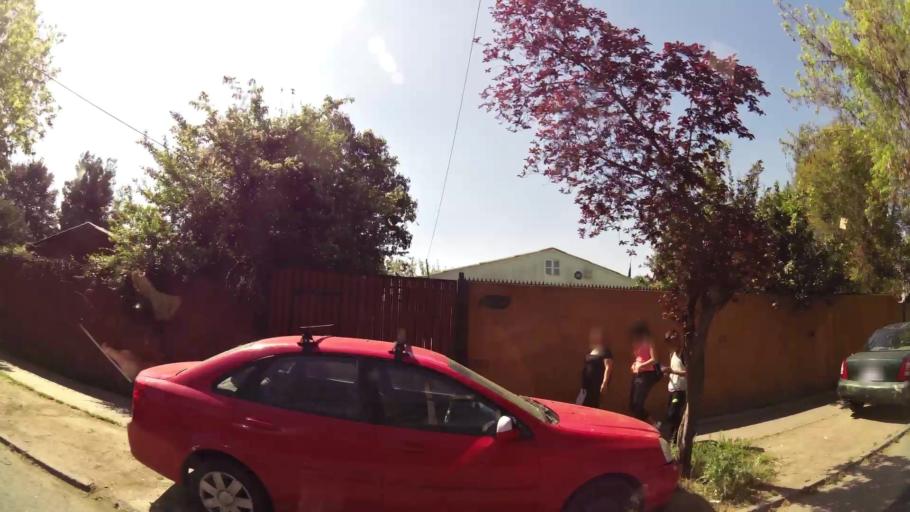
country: CL
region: Santiago Metropolitan
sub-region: Provincia de Santiago
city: Villa Presidente Frei, Nunoa, Santiago, Chile
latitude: -33.4864
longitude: -70.5814
